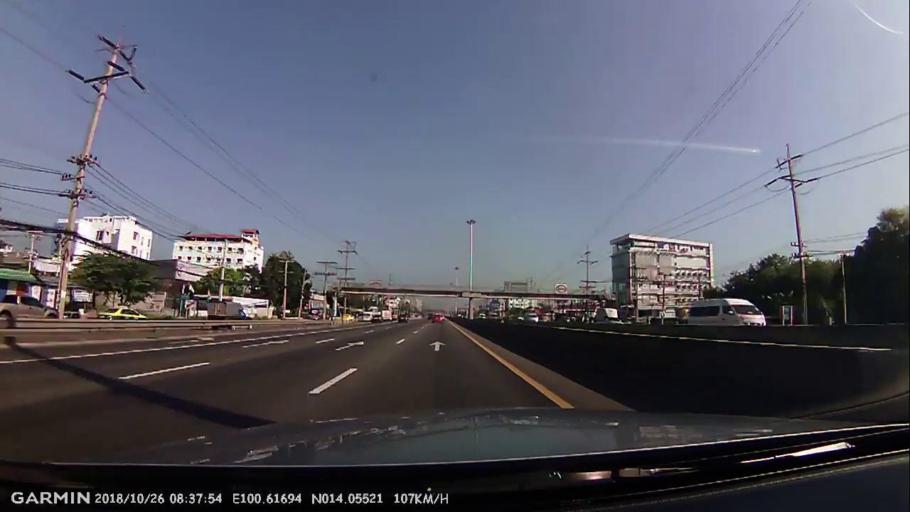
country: TH
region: Pathum Thani
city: Khlong Luang
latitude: 14.0553
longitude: 100.6169
